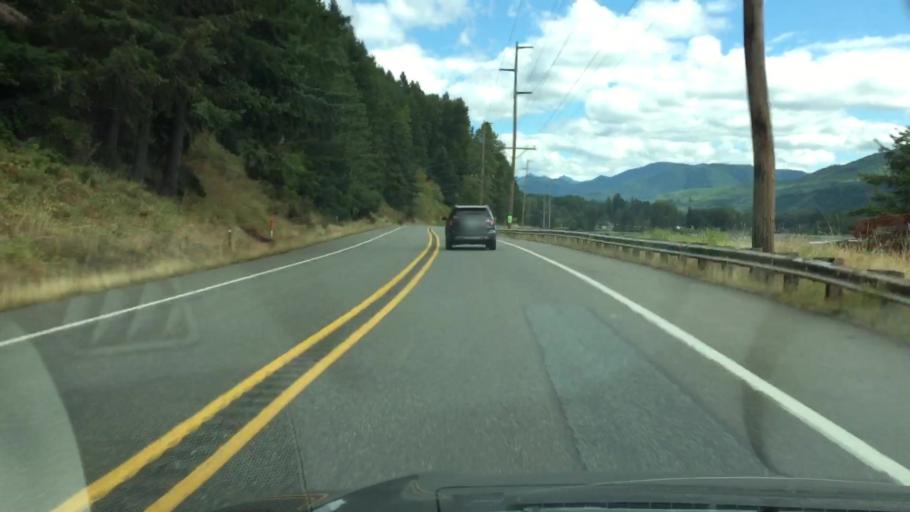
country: US
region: Washington
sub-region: Pierce County
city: Eatonville
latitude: 46.7711
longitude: -122.2117
